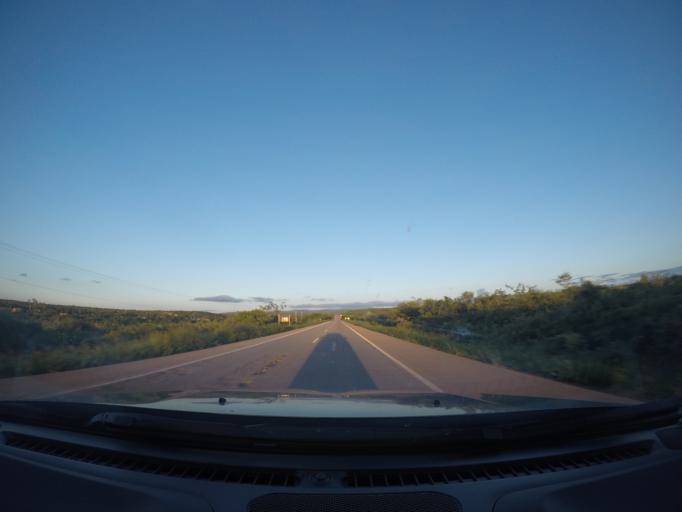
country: BR
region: Bahia
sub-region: Seabra
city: Seabra
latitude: -12.3976
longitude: -41.9365
